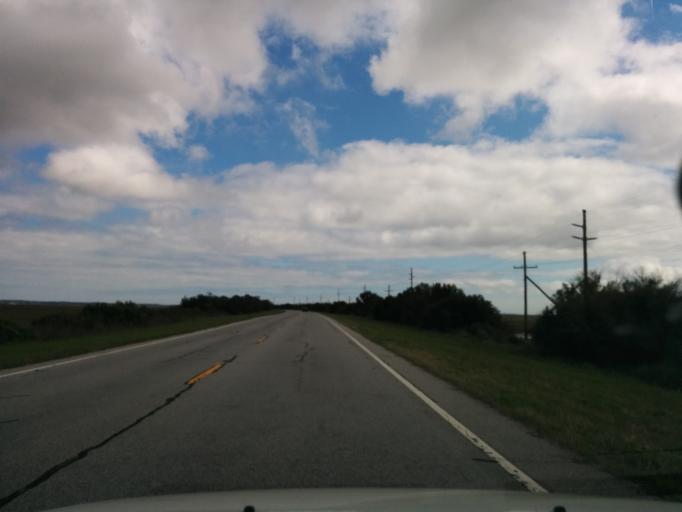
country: US
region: Georgia
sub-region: Glynn County
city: Brunswick
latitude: 31.0793
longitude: -81.4722
